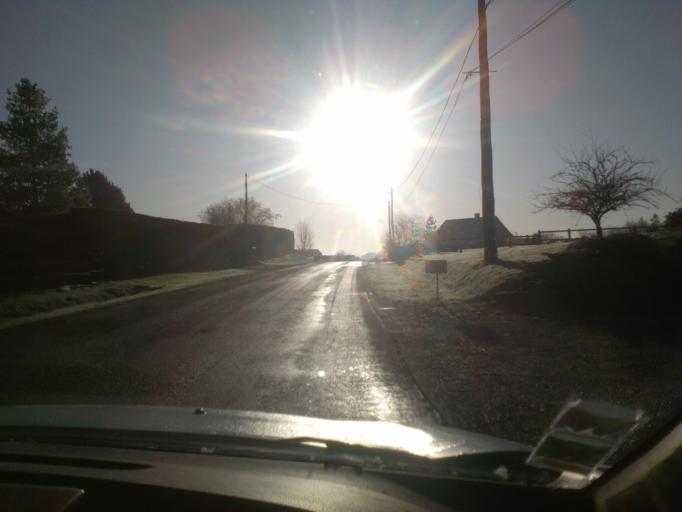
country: FR
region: Lorraine
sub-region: Departement des Vosges
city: Uzemain
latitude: 48.1412
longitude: 6.2506
